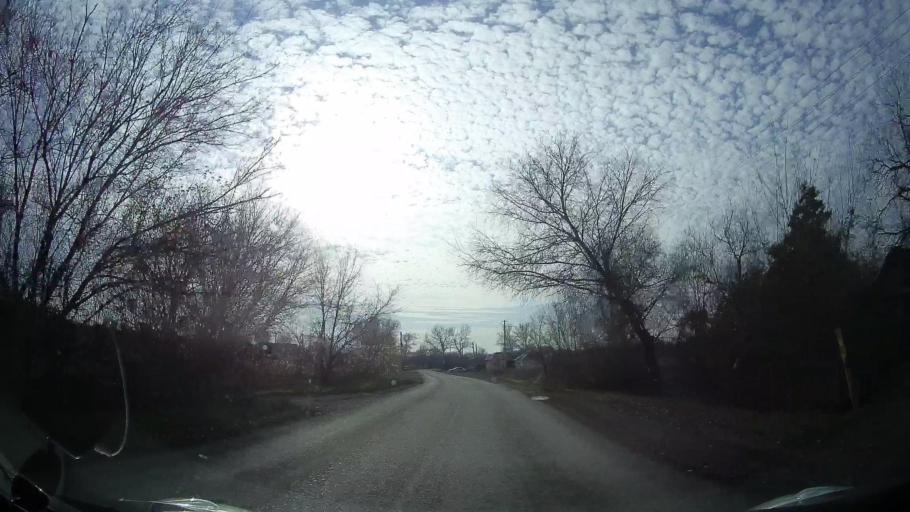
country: RU
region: Rostov
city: Veselyy
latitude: 47.0880
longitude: 40.7395
